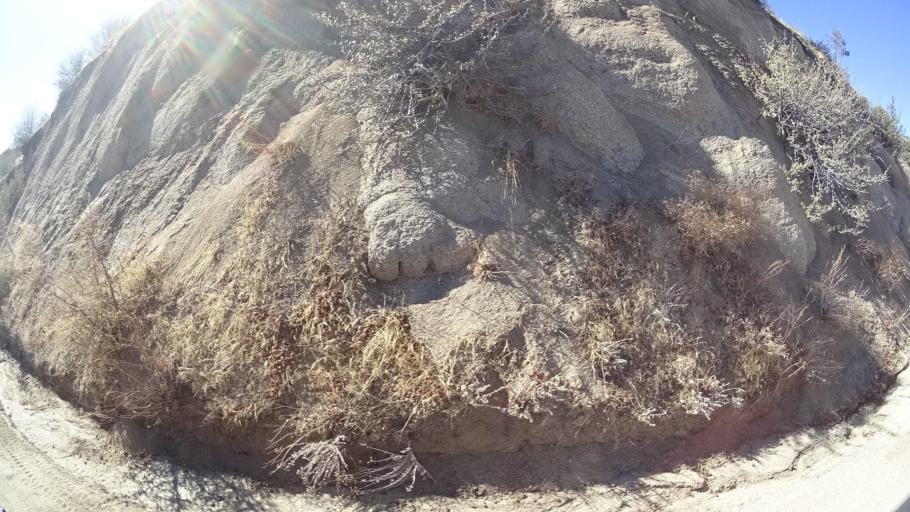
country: US
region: California
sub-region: Kern County
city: Alta Sierra
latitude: 35.7093
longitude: -118.5066
